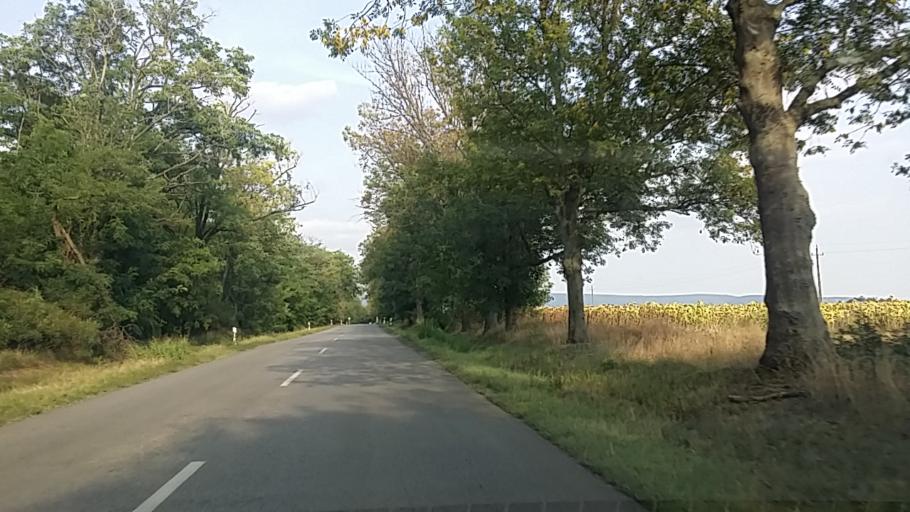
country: HU
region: Komarom-Esztergom
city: Tata
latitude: 47.6280
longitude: 18.2726
